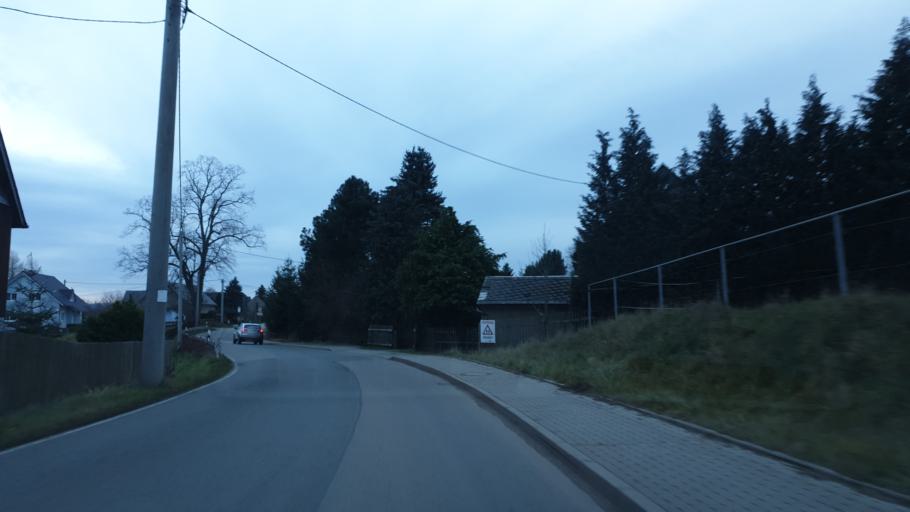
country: DE
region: Saxony
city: Hartenstein
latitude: 50.6888
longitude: 12.6705
